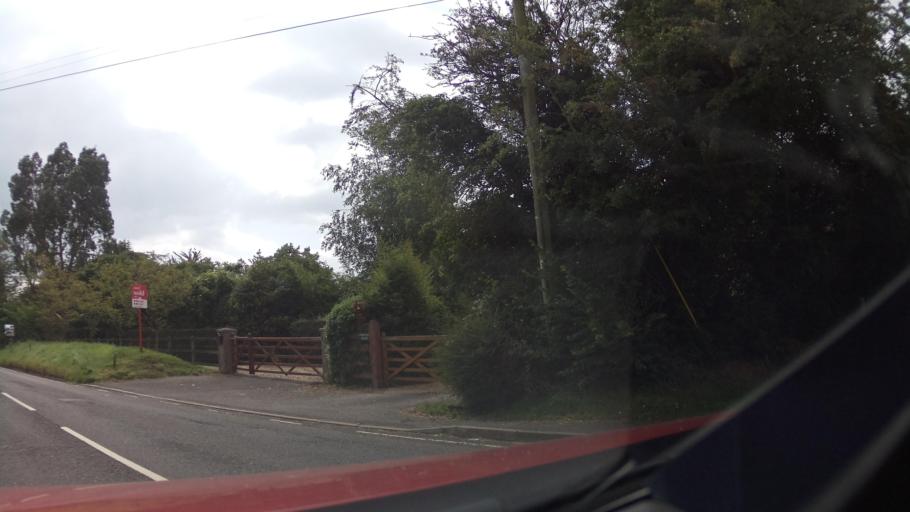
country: GB
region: England
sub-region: Dorset
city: Stalbridge
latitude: 50.9966
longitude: -2.4151
